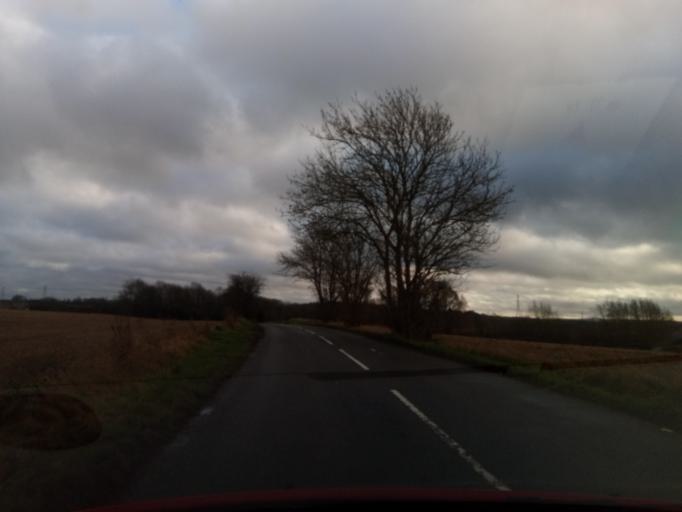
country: GB
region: England
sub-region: Derbyshire
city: Melbourne
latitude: 52.8525
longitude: -1.4333
